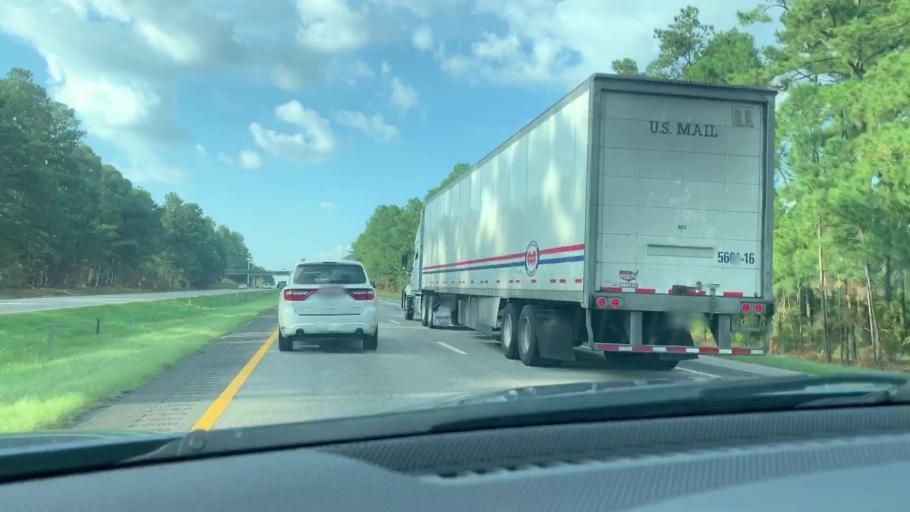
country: US
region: South Carolina
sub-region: Calhoun County
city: Oak Grove
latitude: 33.6978
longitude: -80.9139
